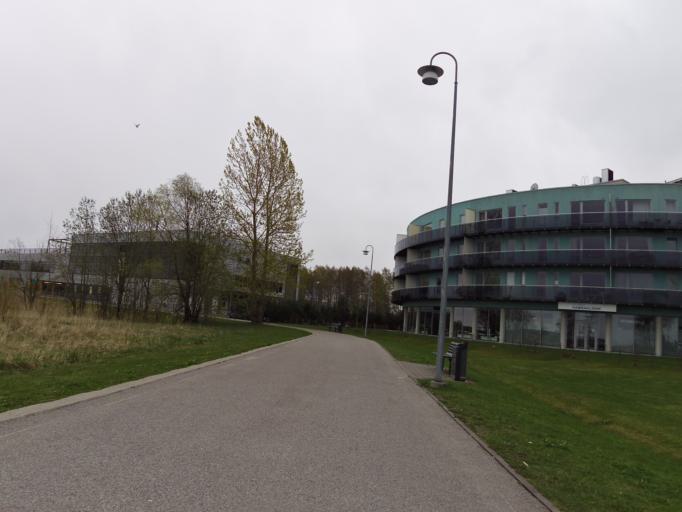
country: EE
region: Harju
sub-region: Saue vald
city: Laagri
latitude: 59.4283
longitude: 24.6626
